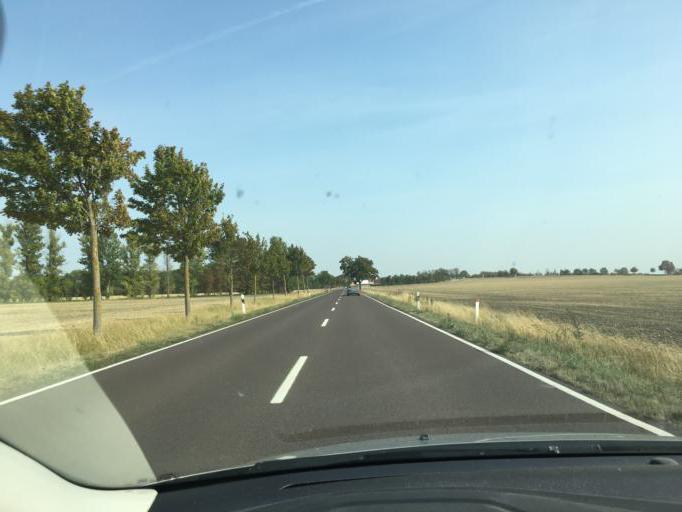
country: DE
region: Saxony-Anhalt
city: Wulfen
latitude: 51.7788
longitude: 11.8976
